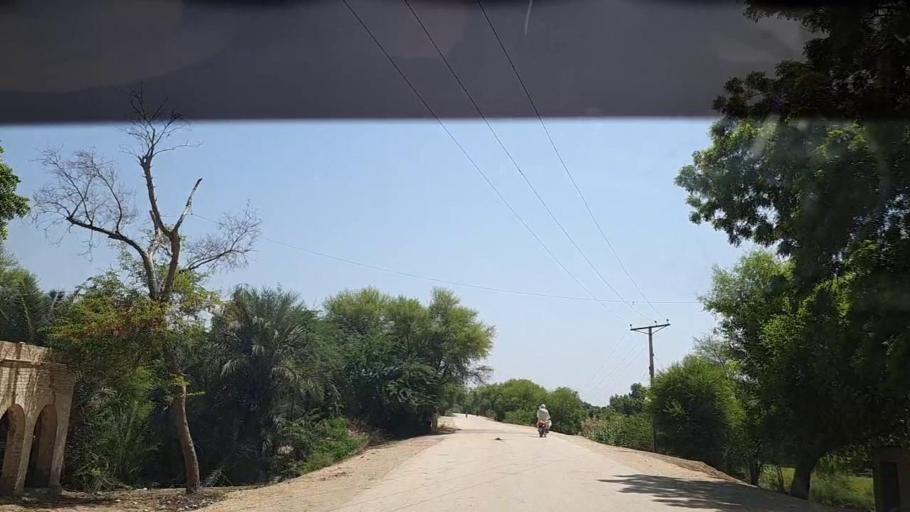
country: PK
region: Sindh
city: Ghauspur
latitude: 28.1638
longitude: 69.1383
